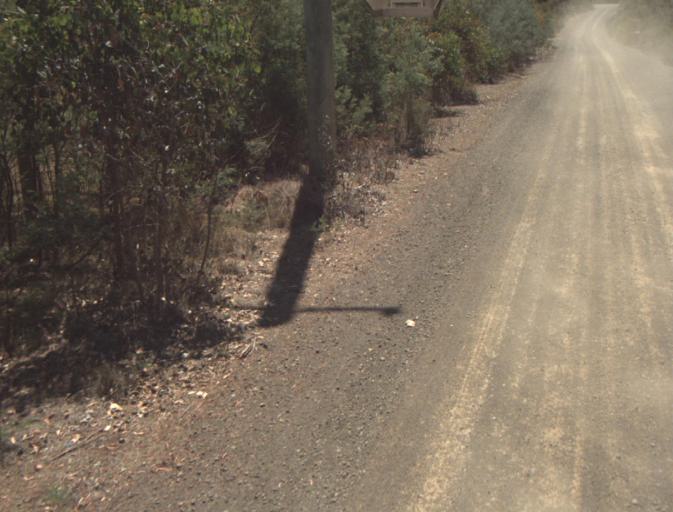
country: AU
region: Tasmania
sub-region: Launceston
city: Mayfield
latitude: -41.2741
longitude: 147.0992
